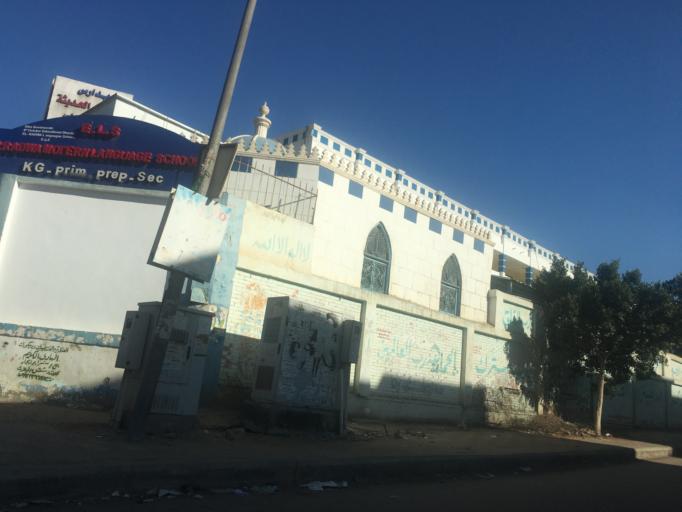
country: EG
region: Al Jizah
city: Madinat Sittah Uktubar
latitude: 29.9791
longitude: 30.9442
